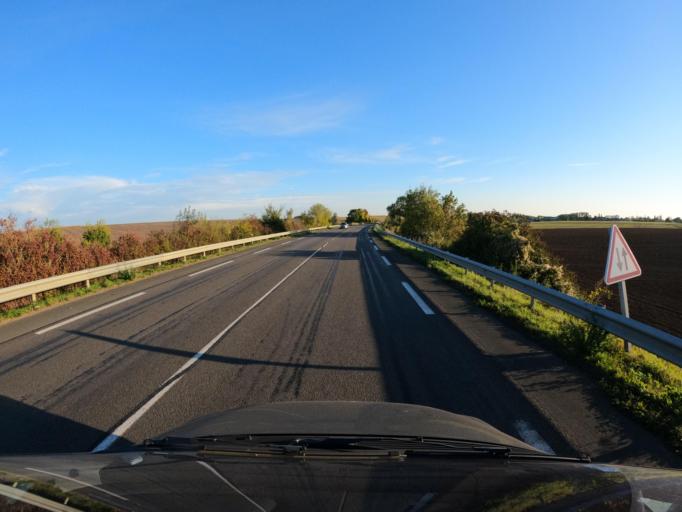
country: FR
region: Pays de la Loire
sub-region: Departement de la Vendee
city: Sainte-Hermine
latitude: 46.5668
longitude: -1.0481
